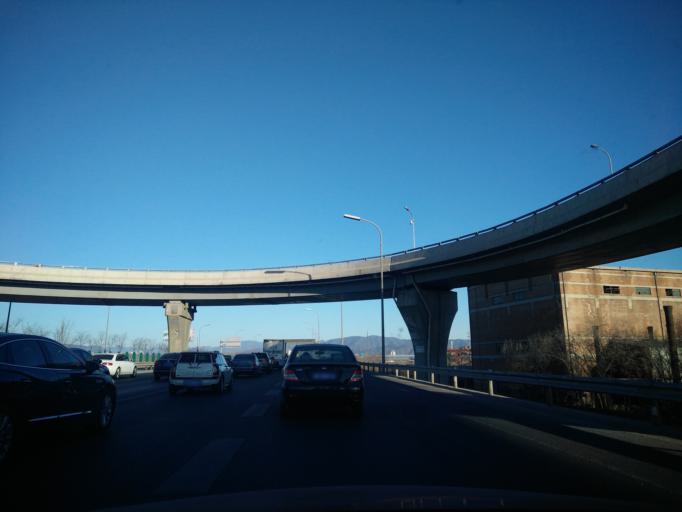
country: CN
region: Beijing
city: Lugu
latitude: 39.8678
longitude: 116.2055
